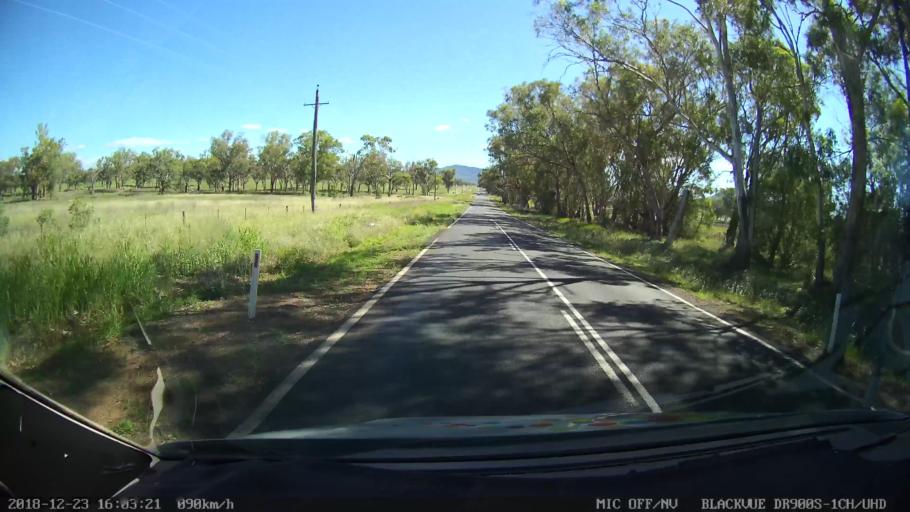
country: AU
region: New South Wales
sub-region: Tamworth Municipality
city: Phillip
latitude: -31.2425
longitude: 150.8014
